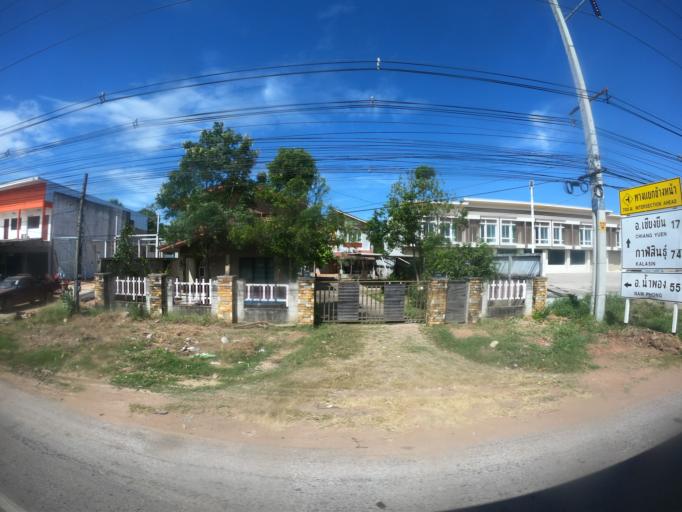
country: TH
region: Khon Kaen
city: Khon Kaen
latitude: 16.4439
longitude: 102.9467
